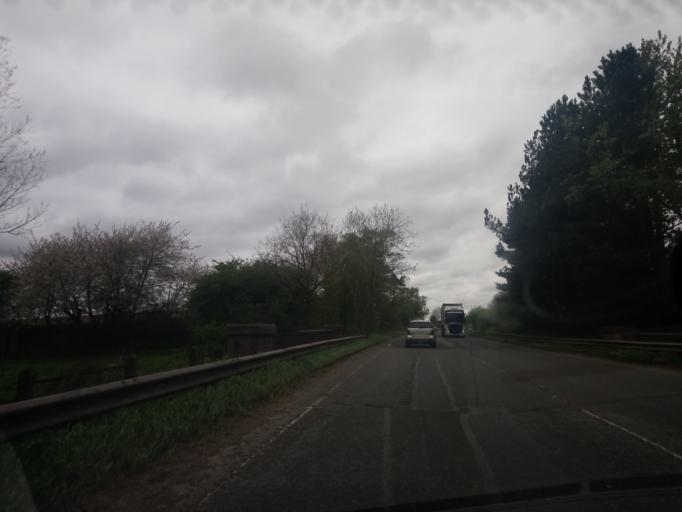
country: GB
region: England
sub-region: Telford and Wrekin
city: Chetwynd
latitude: 52.8106
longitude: -2.4404
